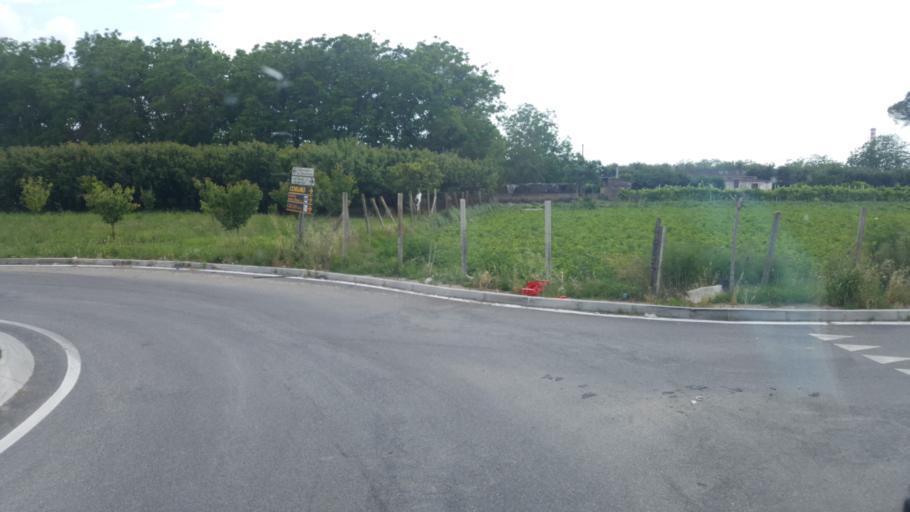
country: IT
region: Campania
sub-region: Provincia di Napoli
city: Acerra
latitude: 40.9736
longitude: 14.3905
